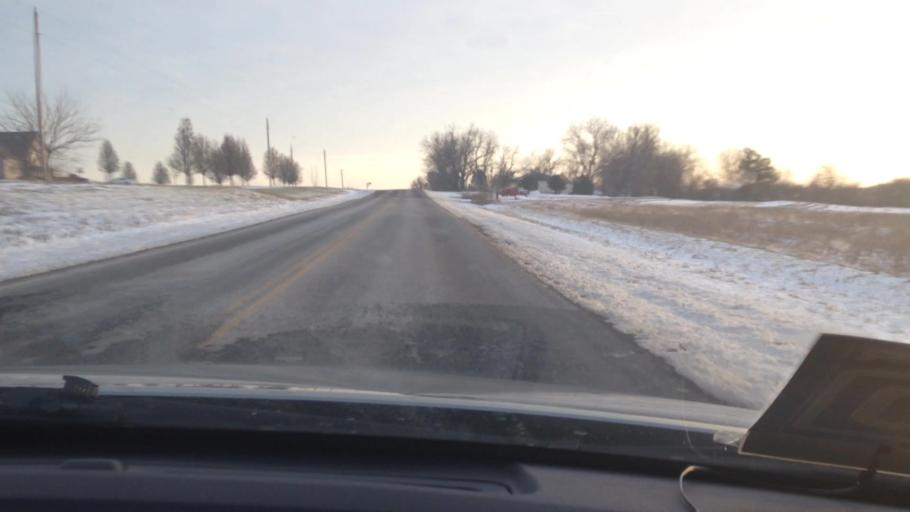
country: US
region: Kansas
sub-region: Leavenworth County
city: Lansing
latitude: 39.2349
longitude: -94.9751
